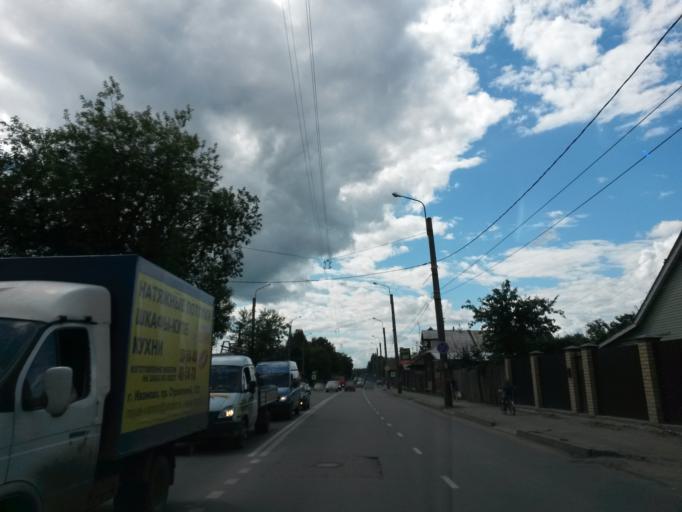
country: RU
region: Ivanovo
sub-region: Gorod Ivanovo
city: Ivanovo
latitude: 56.9923
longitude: 40.9655
